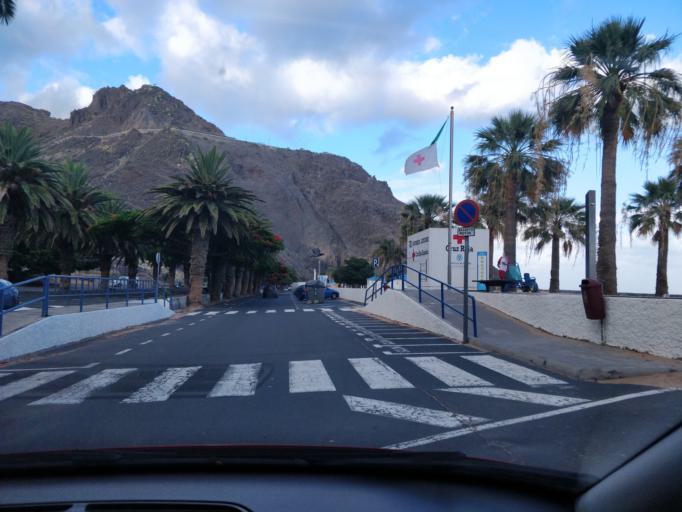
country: ES
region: Canary Islands
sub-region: Provincia de Santa Cruz de Tenerife
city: Santa Cruz de Tenerife
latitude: 28.5101
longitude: -16.1849
